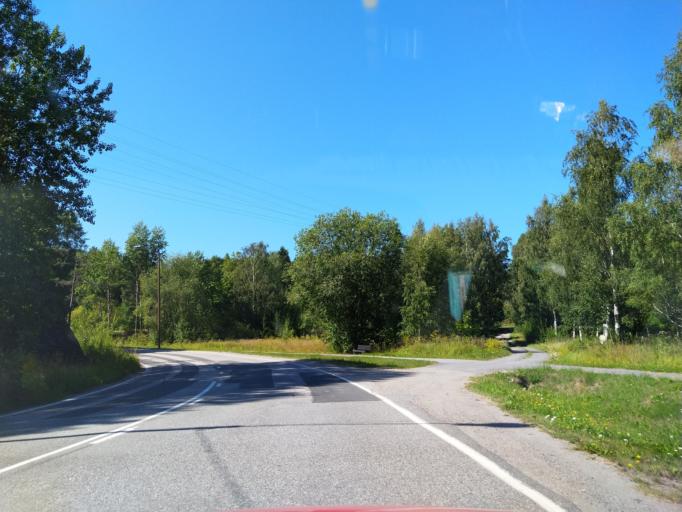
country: FI
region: Varsinais-Suomi
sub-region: Aboland-Turunmaa
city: Dragsfjaerd
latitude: 60.0203
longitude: 22.4967
